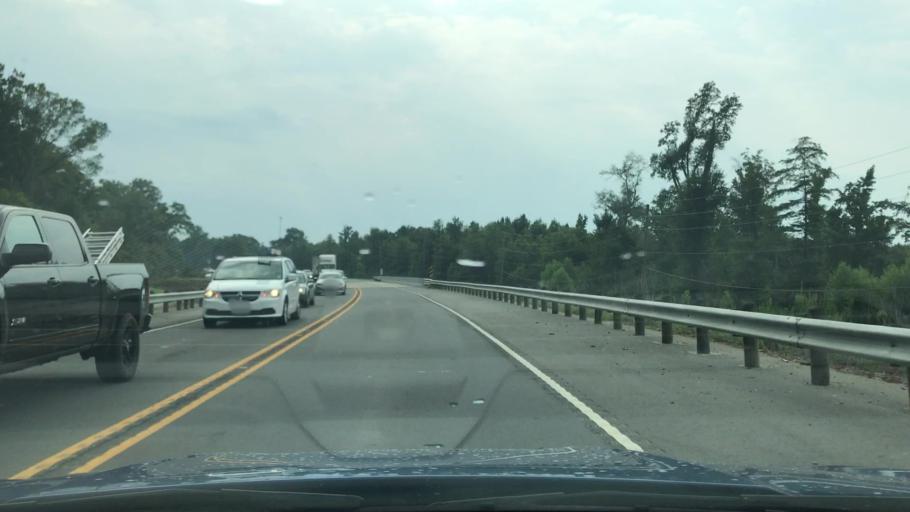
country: US
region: Louisiana
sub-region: Caddo Parish
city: Greenwood
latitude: 32.4564
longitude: -94.0145
